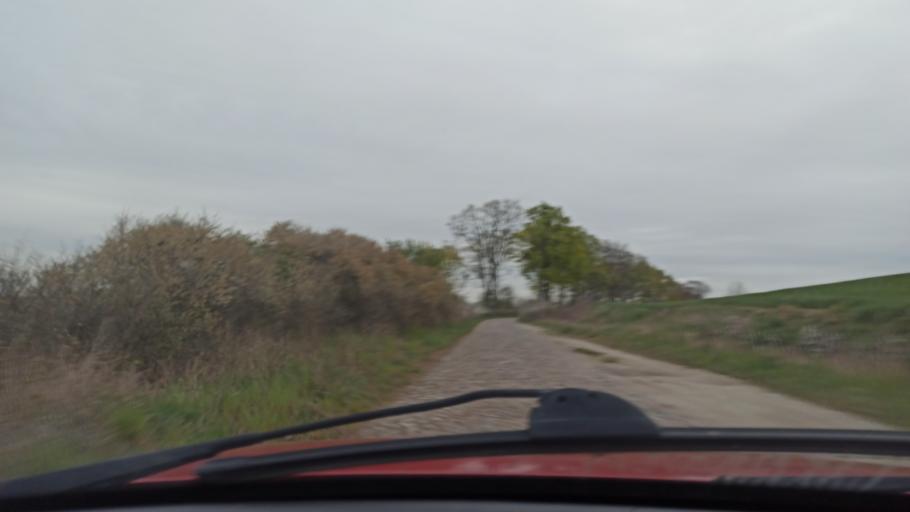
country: PL
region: Kujawsko-Pomorskie
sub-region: Powiat grudziadzki
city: Lasin
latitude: 53.5676
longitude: 19.0777
